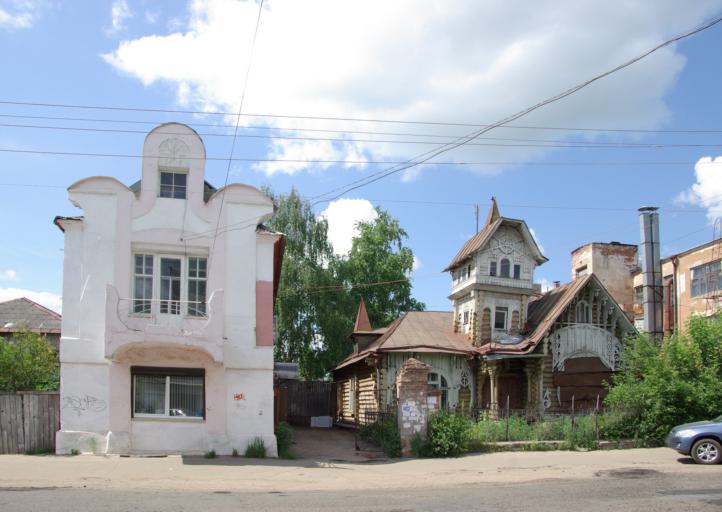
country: RU
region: Tverskaya
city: Kimry
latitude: 56.8720
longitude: 37.3600
